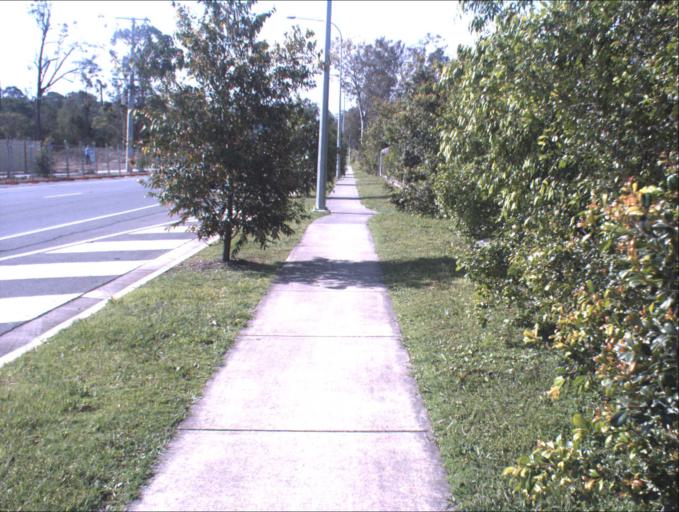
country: AU
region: Queensland
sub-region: Logan
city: Logan City
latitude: -27.6695
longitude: 153.0909
